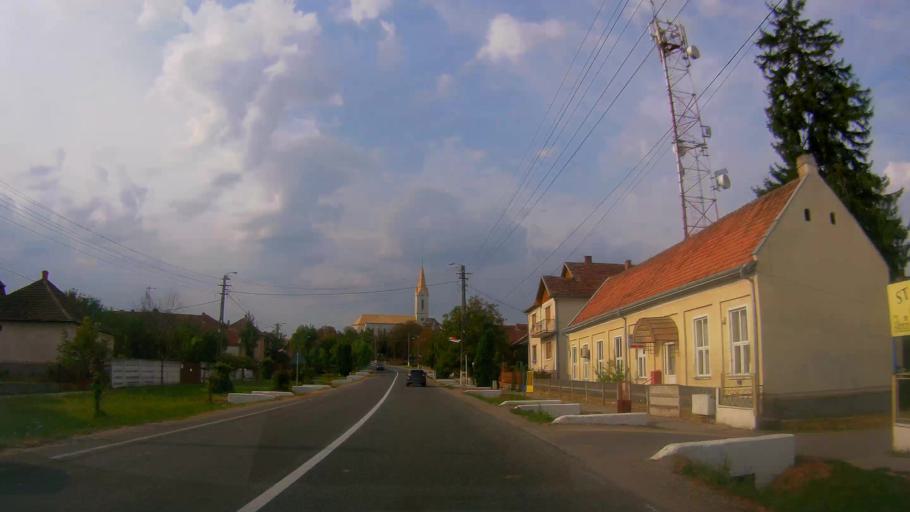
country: RO
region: Satu Mare
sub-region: Oras Ardud
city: Ardud
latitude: 47.6400
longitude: 22.8882
